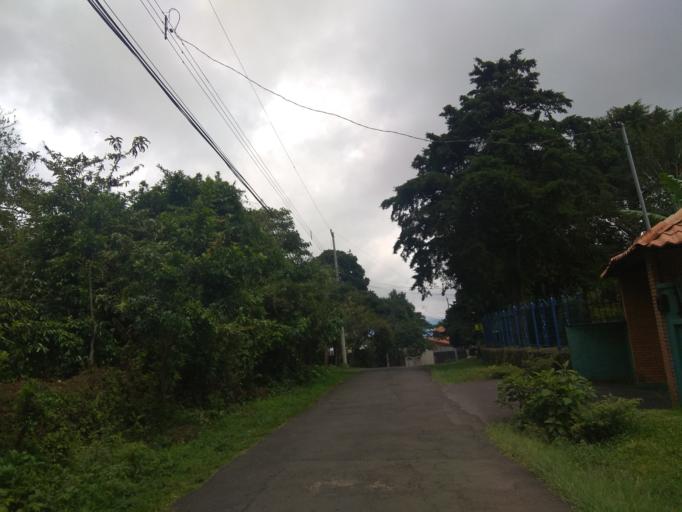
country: CR
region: Heredia
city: San Josecito
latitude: 10.0342
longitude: -84.0969
